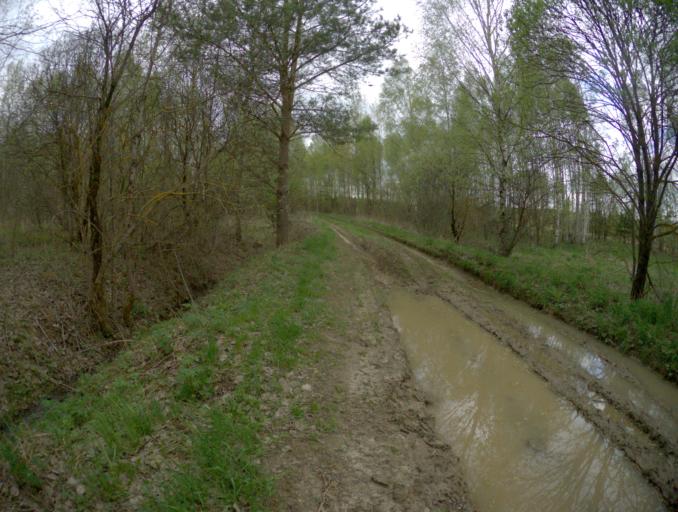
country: RU
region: Vladimir
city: Golovino
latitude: 55.9795
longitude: 40.4219
